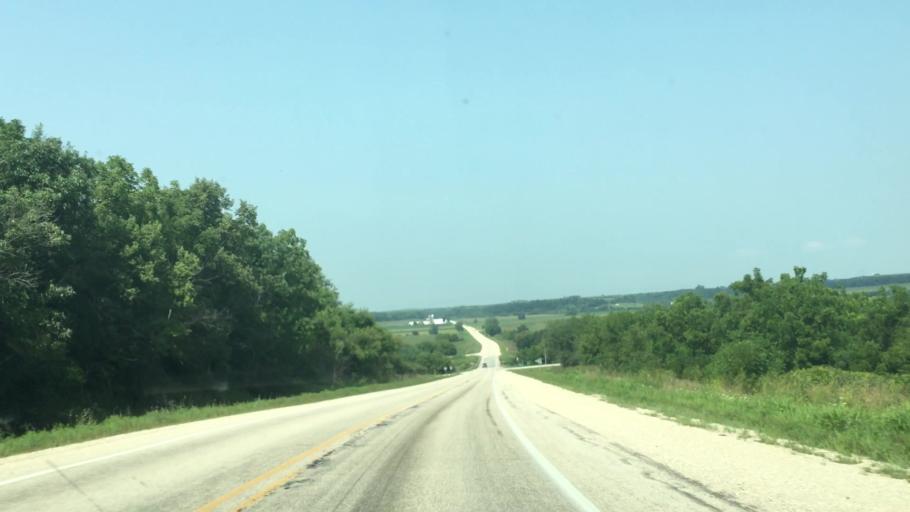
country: US
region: Iowa
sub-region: Fayette County
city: West Union
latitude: 43.0471
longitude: -91.8400
